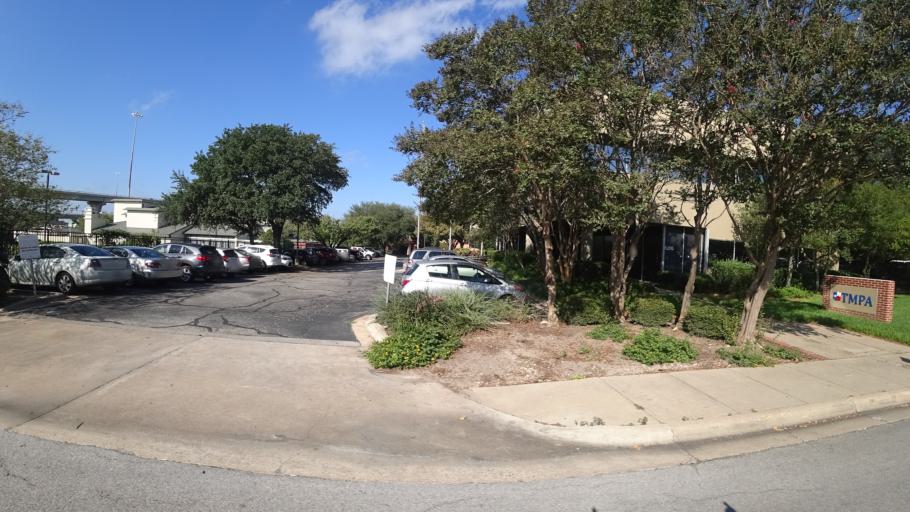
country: US
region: Texas
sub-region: Travis County
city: Austin
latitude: 30.3235
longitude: -97.7030
